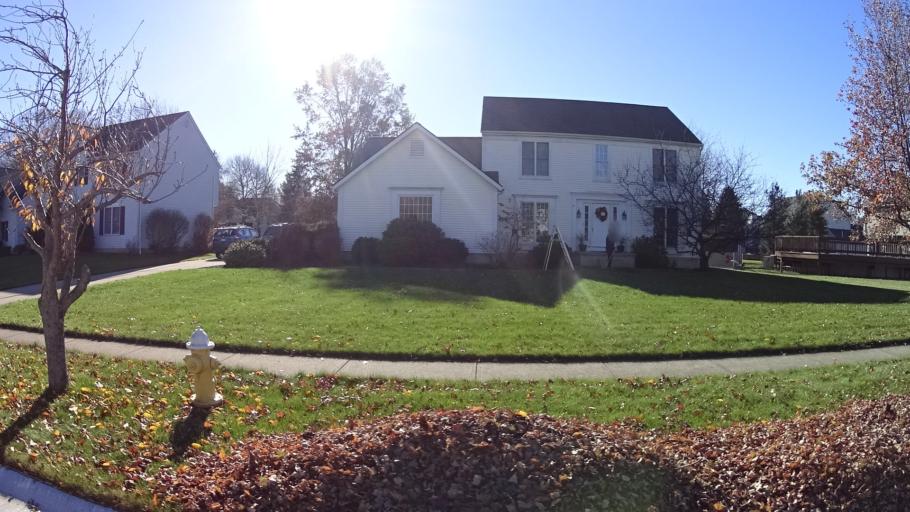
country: US
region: Ohio
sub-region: Lorain County
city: Avon Center
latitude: 41.4868
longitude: -81.9968
